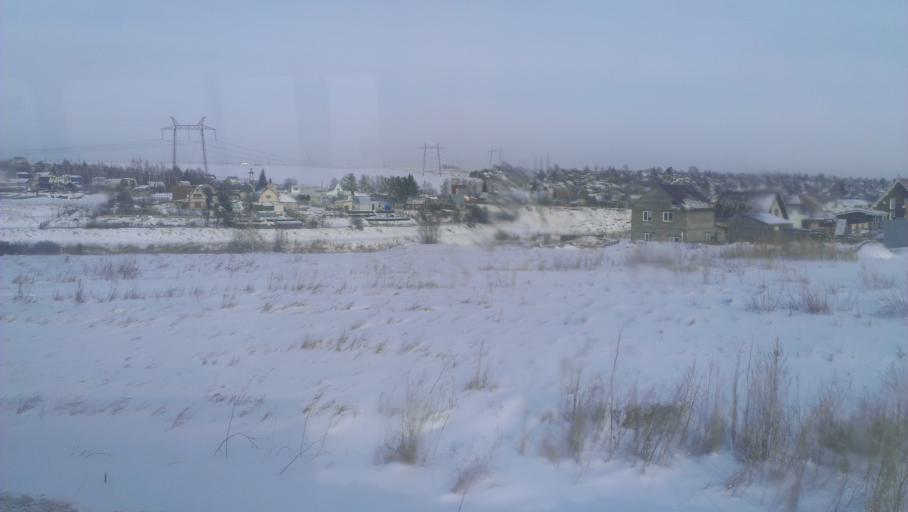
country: RU
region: Altai Krai
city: Gon'ba
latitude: 53.4139
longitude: 83.5520
